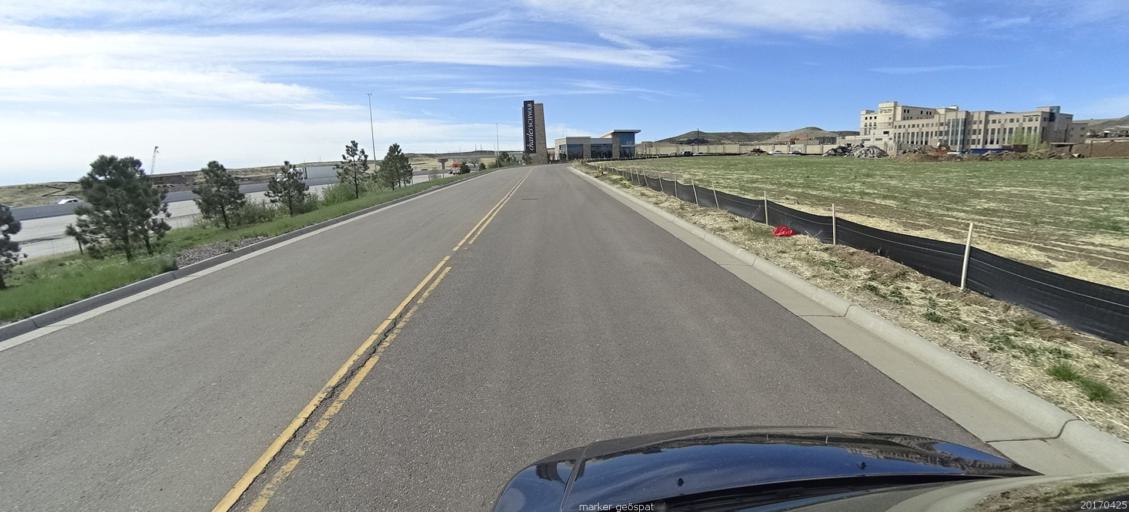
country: US
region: Colorado
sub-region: Douglas County
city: Meridian
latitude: 39.5333
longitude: -104.8690
